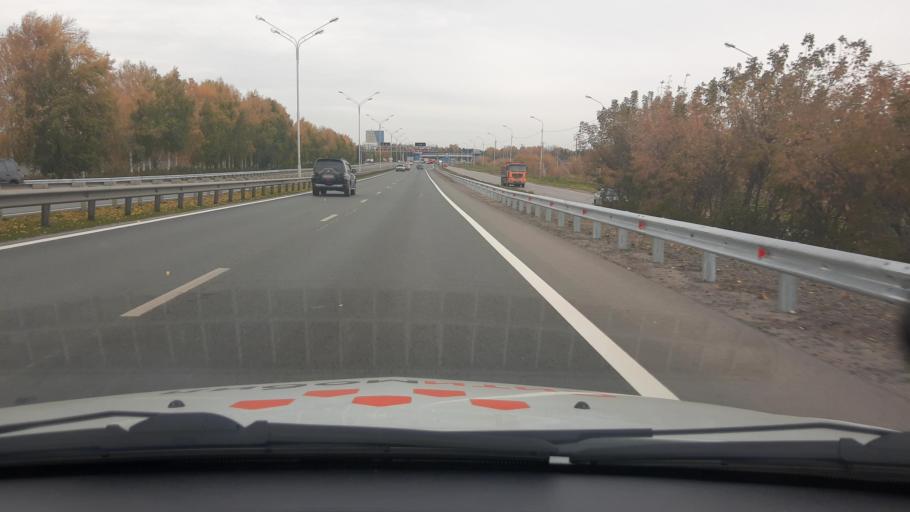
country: RU
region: Bashkortostan
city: Ufa
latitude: 54.5825
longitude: 55.9155
